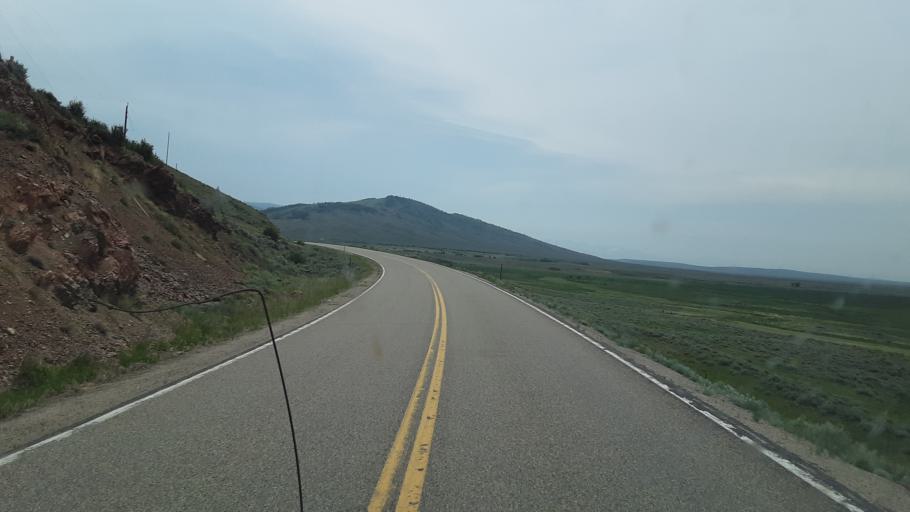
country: US
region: Colorado
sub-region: Jackson County
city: Walden
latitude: 40.9187
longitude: -106.3101
